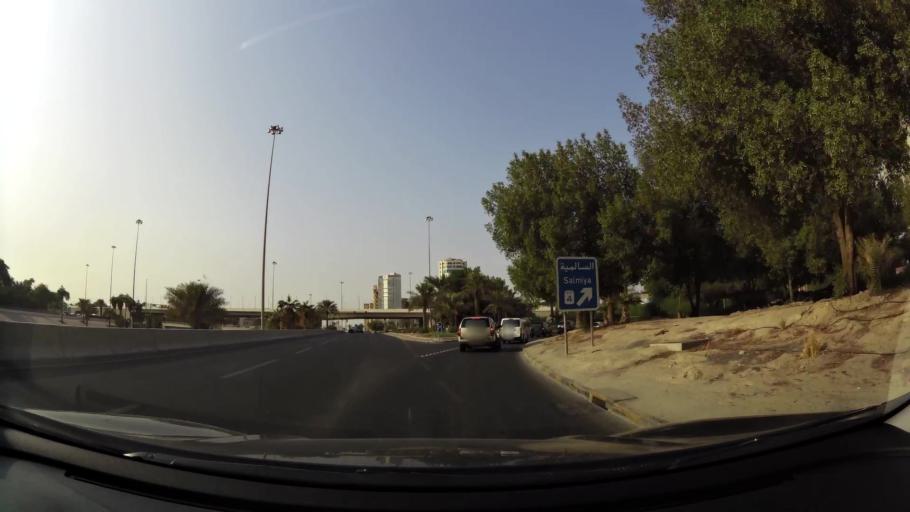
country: KW
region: Muhafazat Hawalli
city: Hawalli
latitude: 29.3219
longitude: 48.0134
